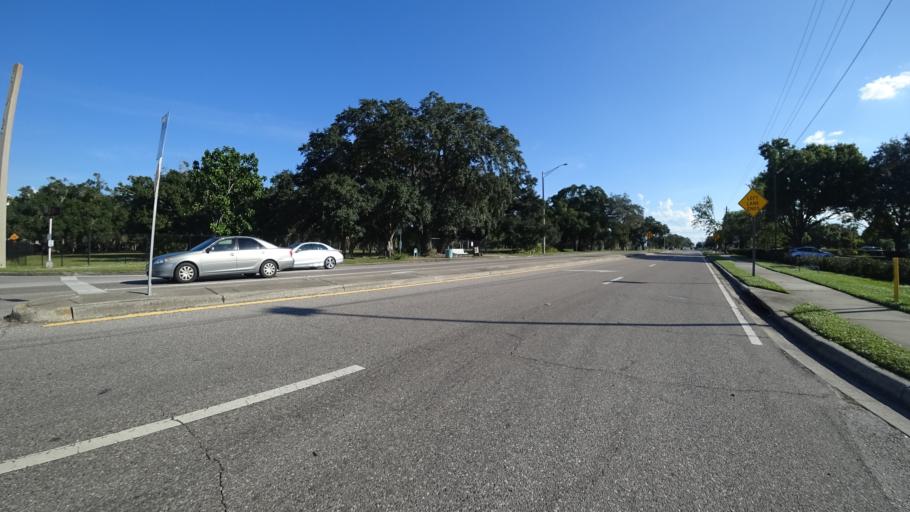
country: US
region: Florida
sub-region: Manatee County
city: West Bradenton
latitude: 27.4848
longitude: -82.6205
